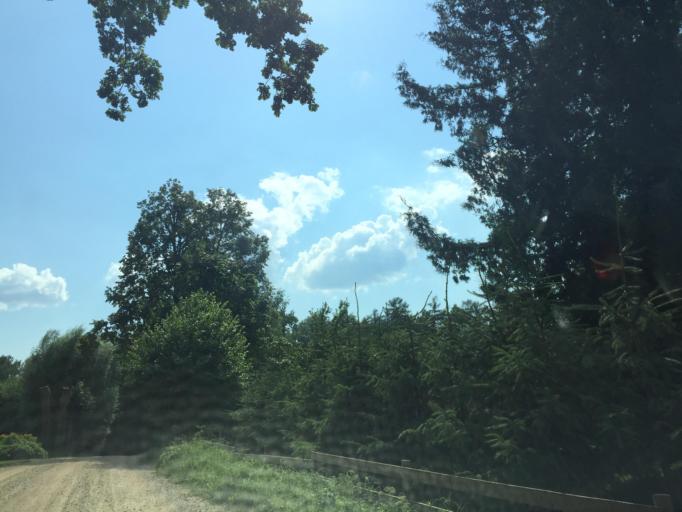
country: LV
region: Pargaujas
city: Stalbe
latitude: 57.3687
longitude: 25.1079
